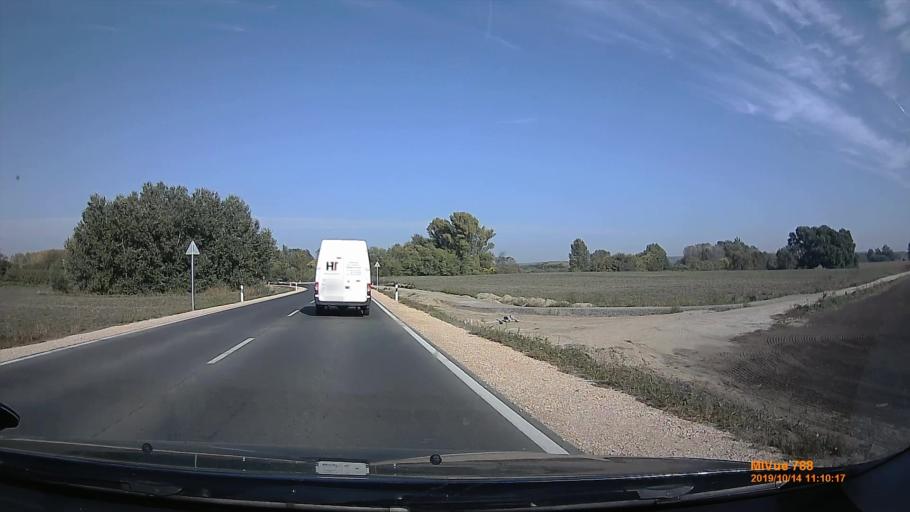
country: HU
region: Pest
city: Peteri
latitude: 47.3740
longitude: 19.4221
